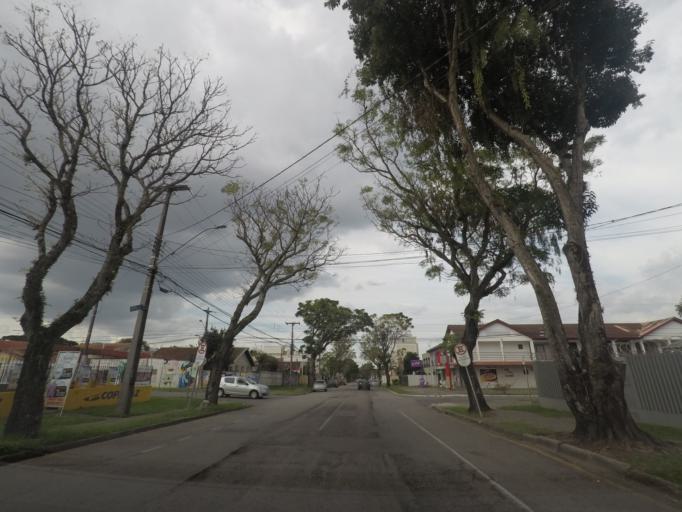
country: BR
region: Parana
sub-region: Curitiba
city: Curitiba
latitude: -25.4830
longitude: -49.2525
